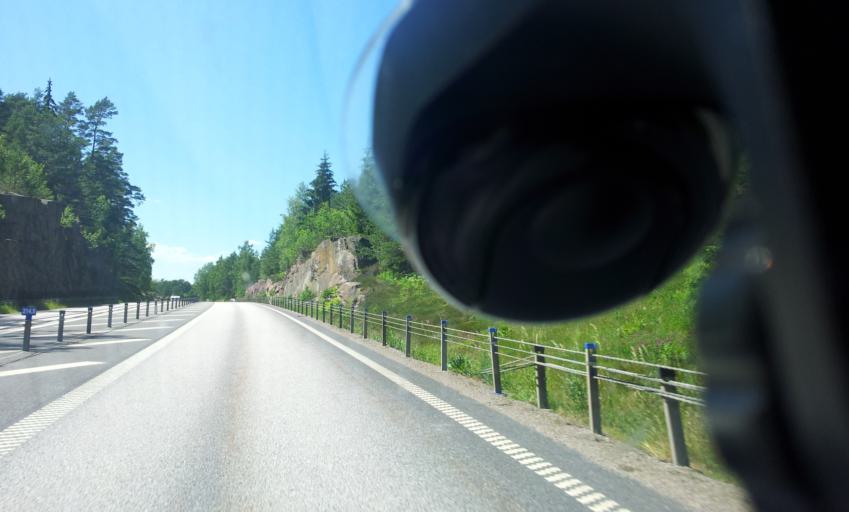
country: SE
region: Kalmar
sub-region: Vasterviks Kommun
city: Forserum
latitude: 57.9678
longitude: 16.4635
